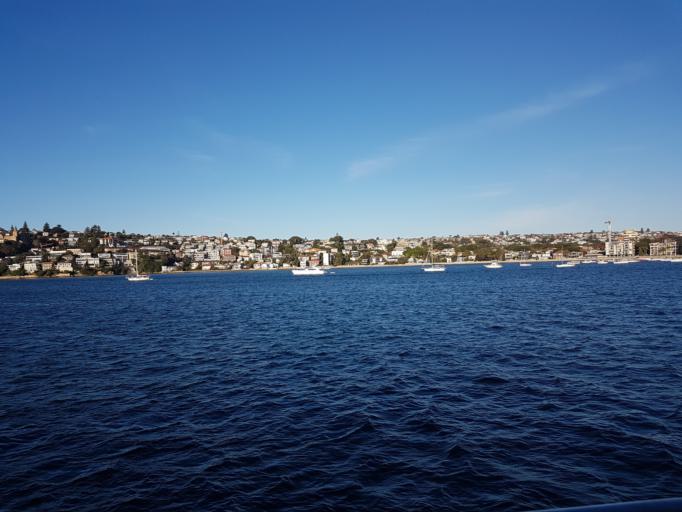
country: AU
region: New South Wales
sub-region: Woollahra
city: Point Piper
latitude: -33.8669
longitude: 151.2612
